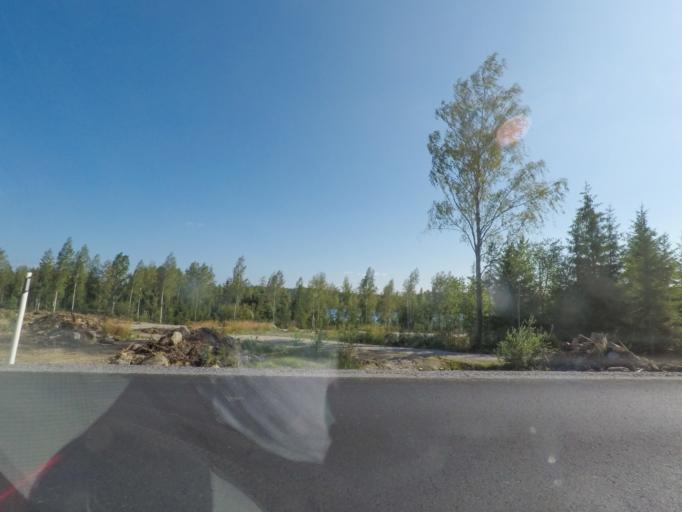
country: FI
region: Southern Savonia
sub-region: Mikkeli
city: Mikkeli
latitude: 61.7576
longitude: 27.5591
